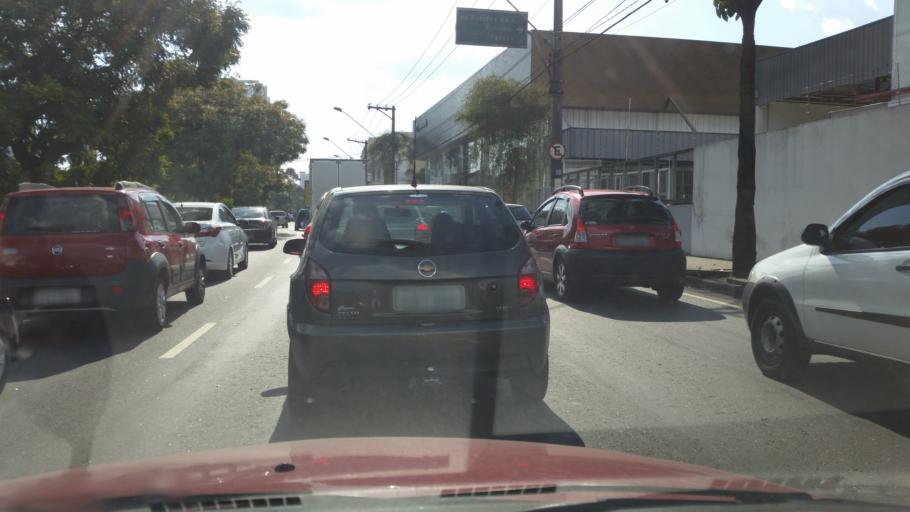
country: BR
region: Sao Paulo
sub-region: Diadema
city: Diadema
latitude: -23.6849
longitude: -46.6158
